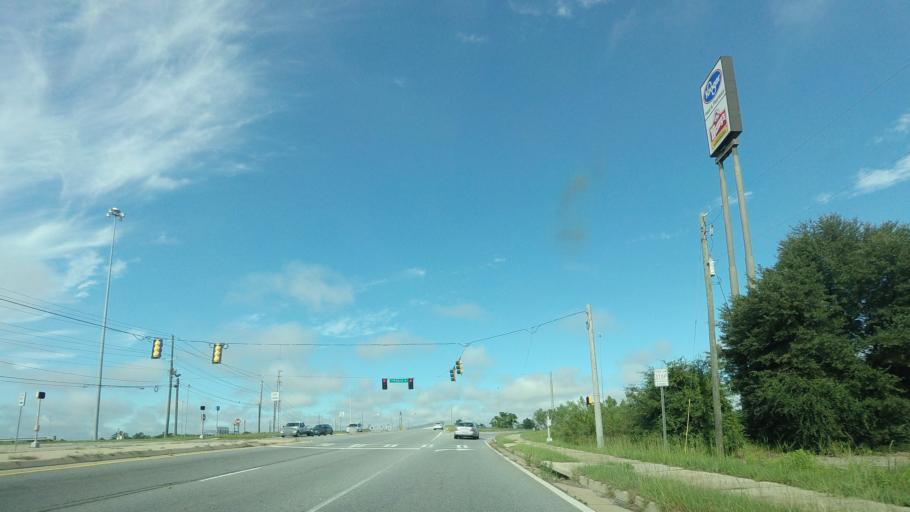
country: US
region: Georgia
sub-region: Peach County
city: Byron
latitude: 32.7440
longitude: -83.7162
